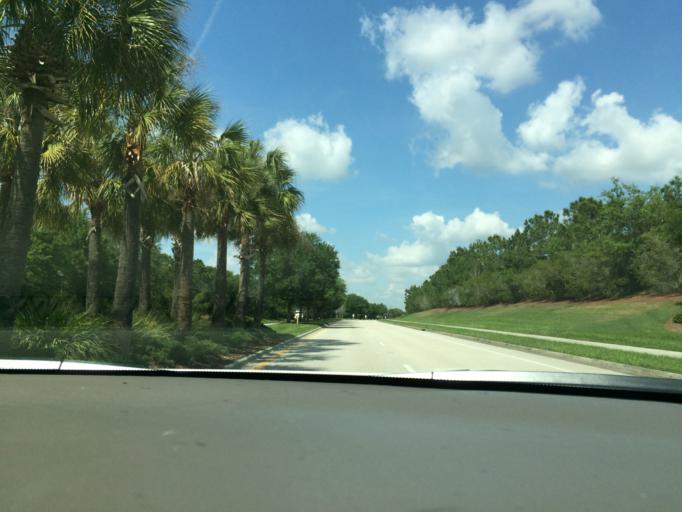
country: US
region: Florida
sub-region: Sarasota County
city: The Meadows
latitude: 27.4200
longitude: -82.3992
